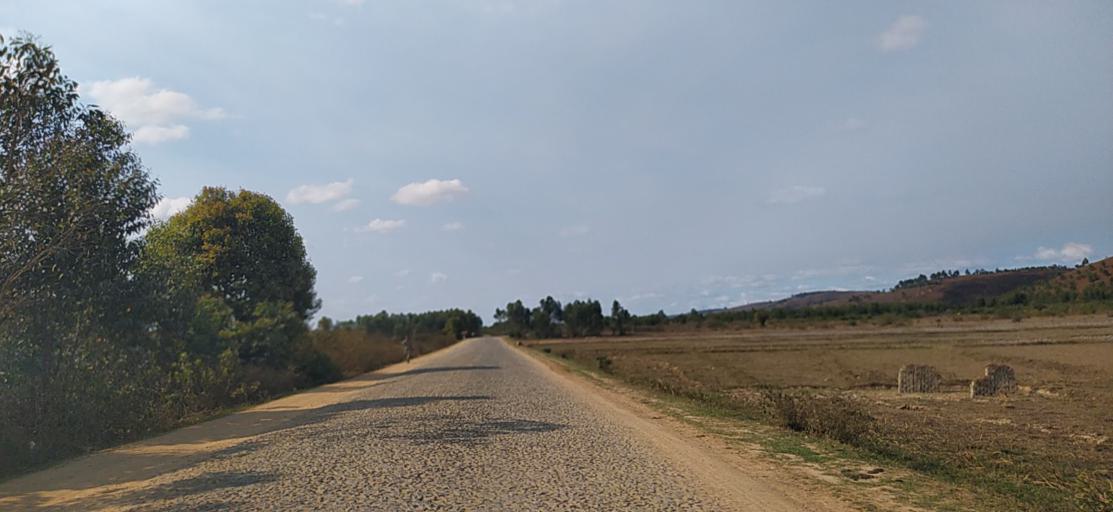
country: MG
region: Alaotra Mangoro
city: Moramanga
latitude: -18.6902
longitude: 48.2711
